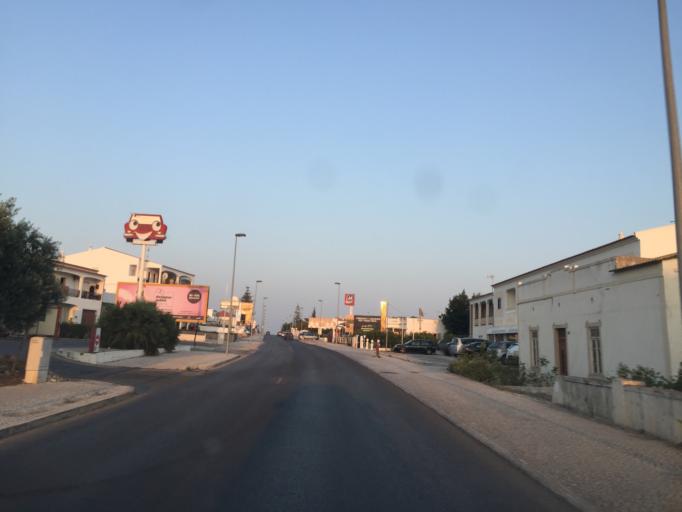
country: PT
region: Faro
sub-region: Loule
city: Almancil
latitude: 37.0845
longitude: -8.0230
